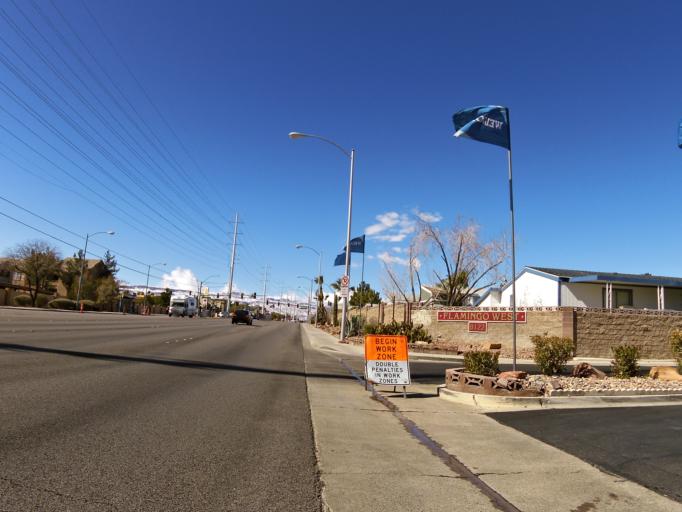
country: US
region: Nevada
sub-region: Clark County
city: Spring Valley
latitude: 36.1147
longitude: -115.2682
